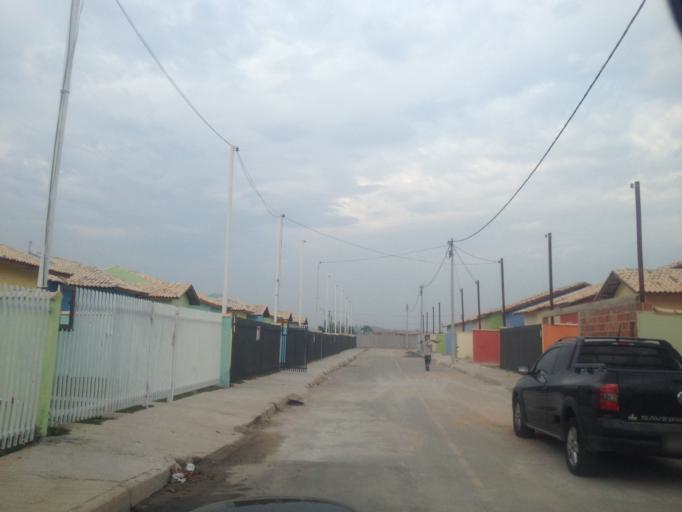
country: BR
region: Rio de Janeiro
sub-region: Porto Real
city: Porto Real
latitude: -22.4204
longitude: -44.3026
